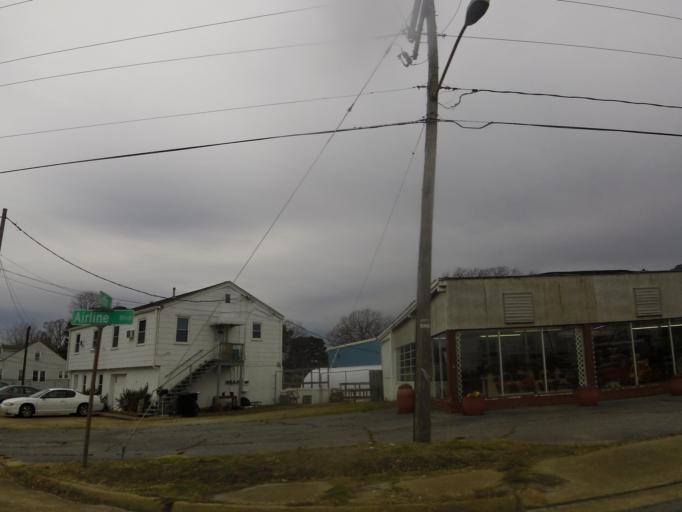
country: US
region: Virginia
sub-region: City of Portsmouth
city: Portsmouth Heights
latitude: 36.8291
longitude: -76.3449
